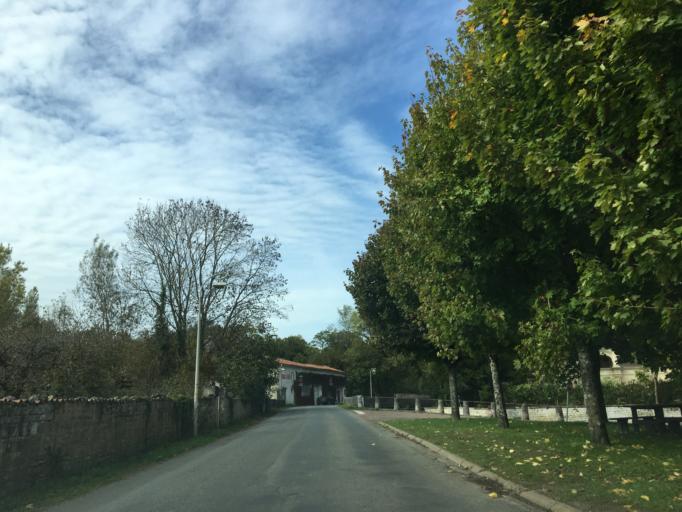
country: FR
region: Poitou-Charentes
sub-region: Departement de la Charente-Maritime
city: Aulnay
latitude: 46.0672
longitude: -0.4154
